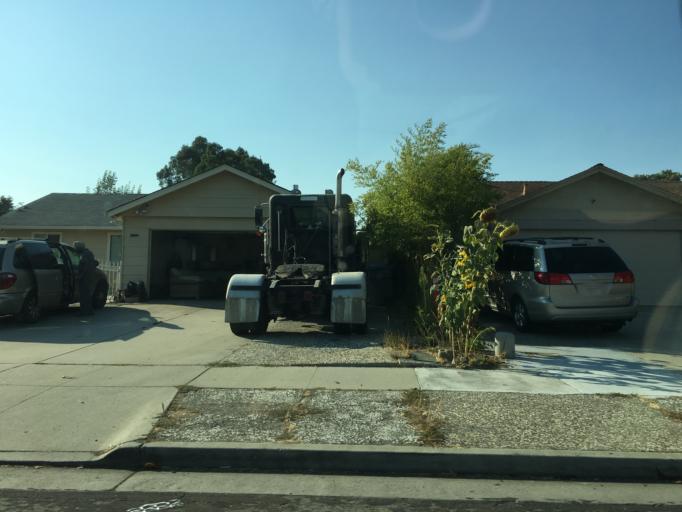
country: US
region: California
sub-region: Santa Clara County
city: Alum Rock
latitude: 37.3925
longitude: -121.8639
